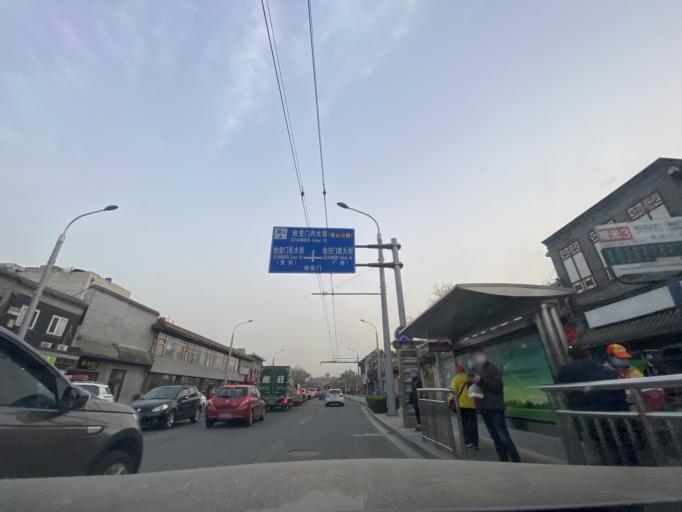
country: CN
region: Beijing
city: Jingshan
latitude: 39.9331
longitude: 116.3899
